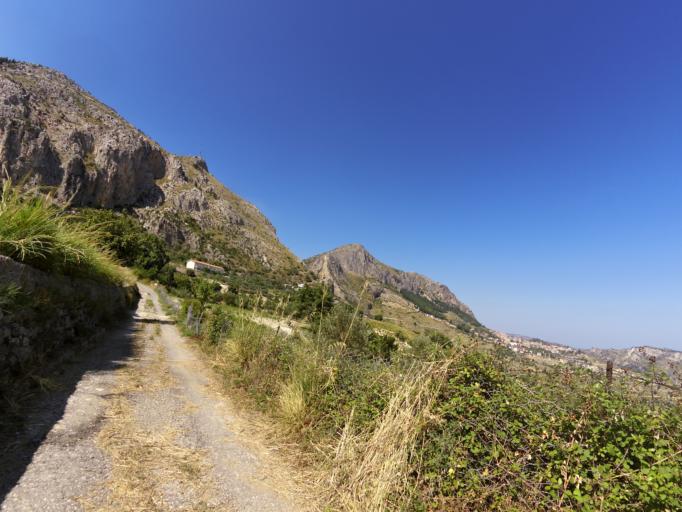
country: IT
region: Calabria
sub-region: Provincia di Reggio Calabria
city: Pazzano
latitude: 38.4640
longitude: 16.4545
